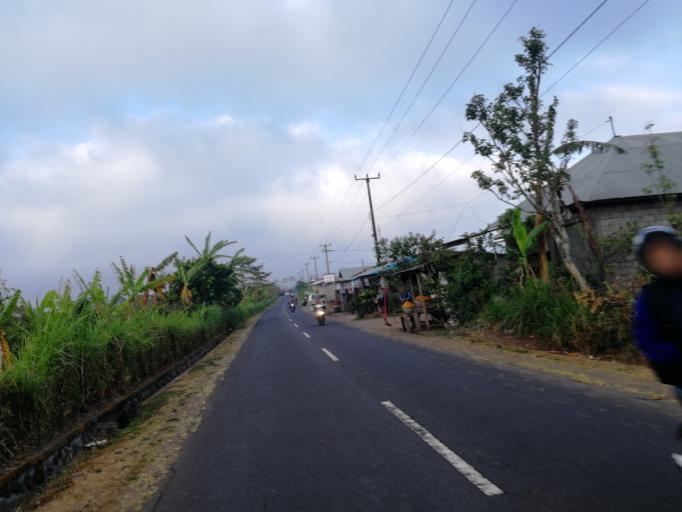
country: ID
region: Bali
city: Banjar Kedisan
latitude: -8.2223
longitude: 115.2645
